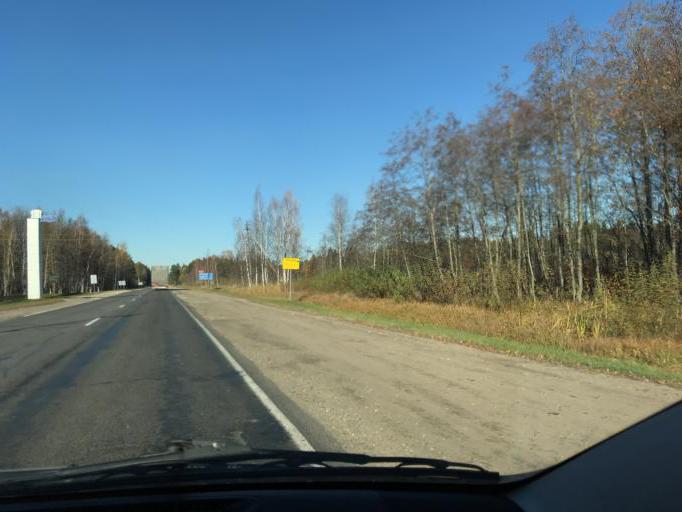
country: BY
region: Vitebsk
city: Polatsk
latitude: 55.5078
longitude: 28.7455
